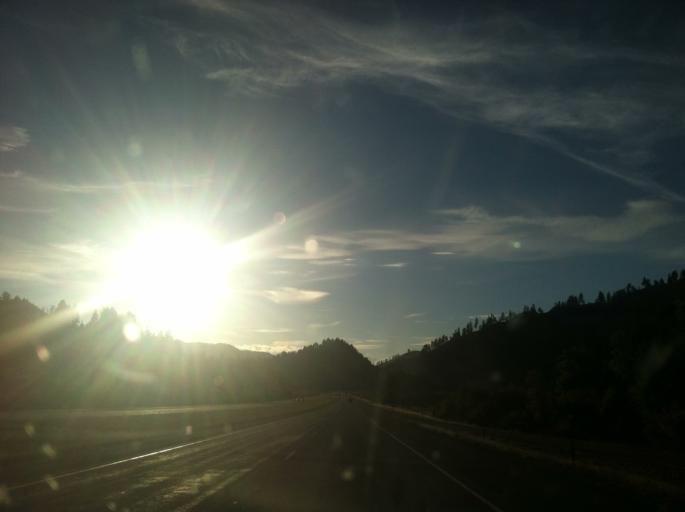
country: US
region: Montana
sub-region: Missoula County
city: Clinton
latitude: 46.6995
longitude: -113.4361
